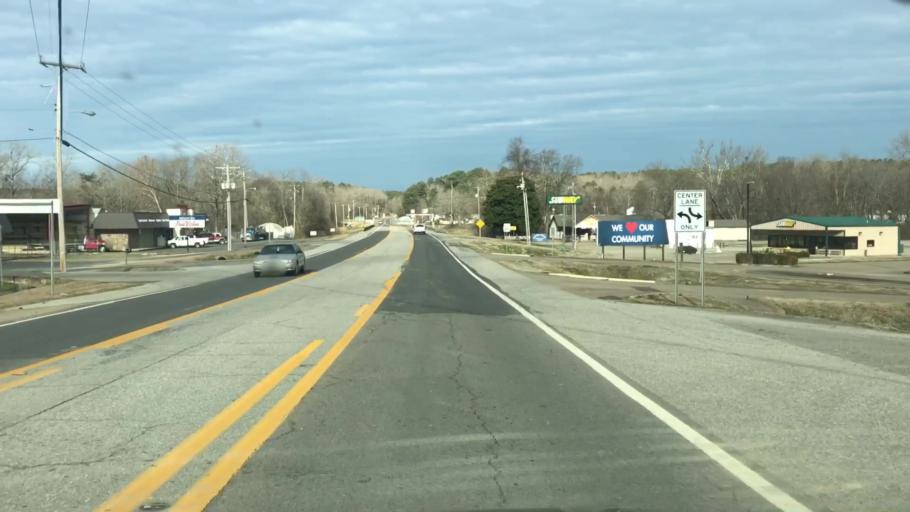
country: US
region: Arkansas
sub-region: Montgomery County
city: Mount Ida
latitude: 34.5590
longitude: -93.6339
